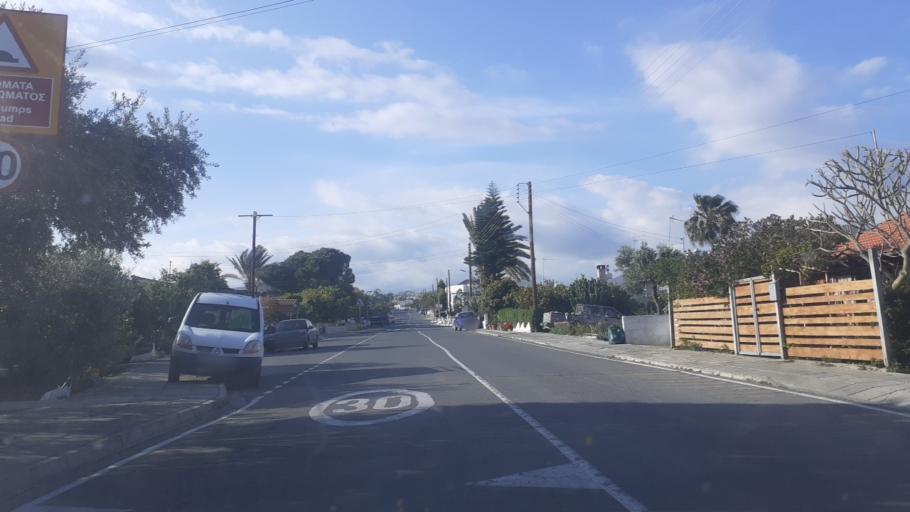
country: CY
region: Larnaka
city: Kolossi
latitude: 34.6782
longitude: 32.9428
